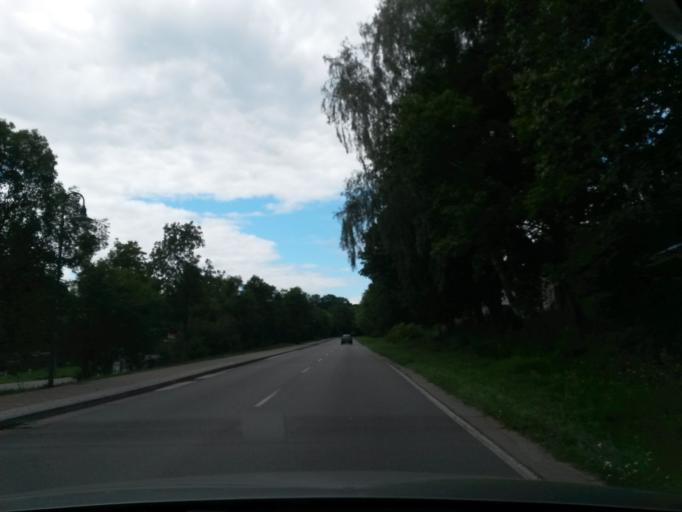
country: DE
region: Brandenburg
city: Oderberg
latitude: 52.8675
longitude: 14.0451
